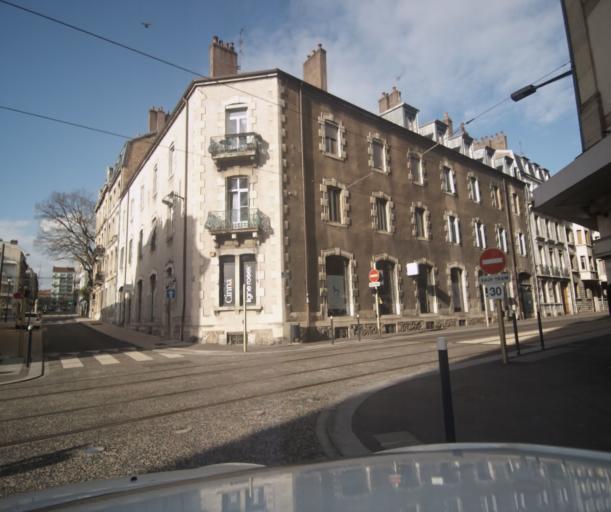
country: FR
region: Franche-Comte
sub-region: Departement du Doubs
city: Besancon
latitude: 47.2438
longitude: 6.0311
